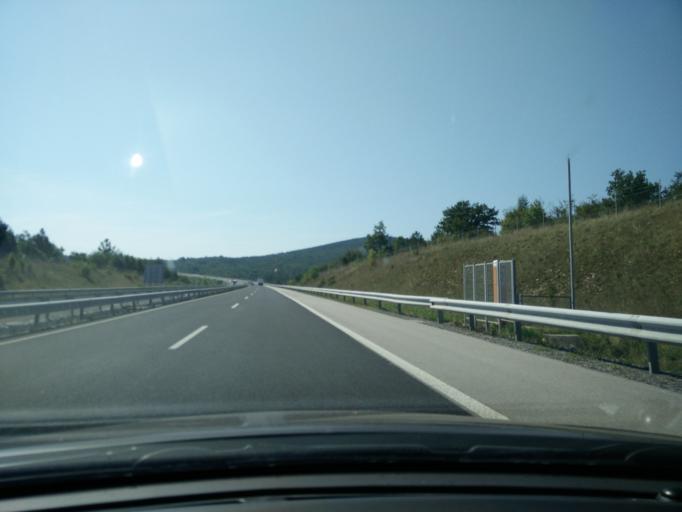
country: SI
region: Divaca
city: Divaca
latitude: 45.6558
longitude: 13.9621
